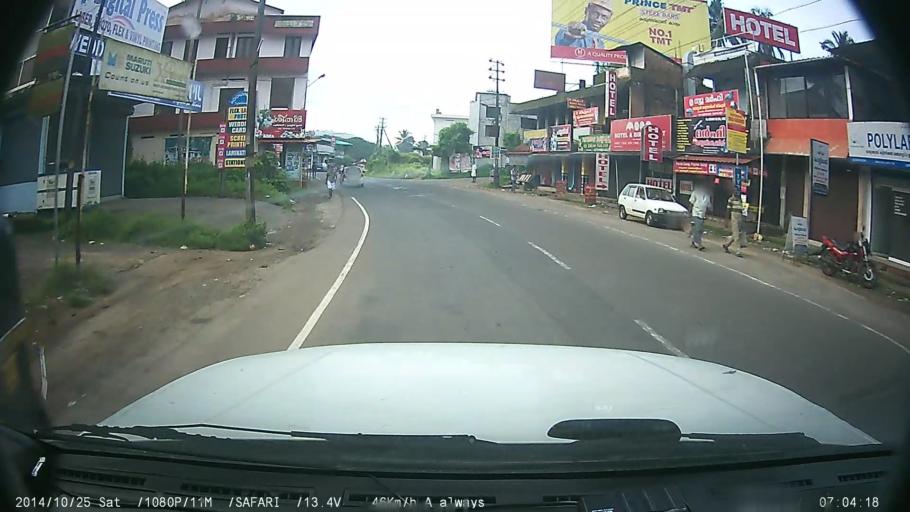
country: IN
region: Kerala
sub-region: Ernakulam
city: Piravam
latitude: 9.8655
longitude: 76.5968
